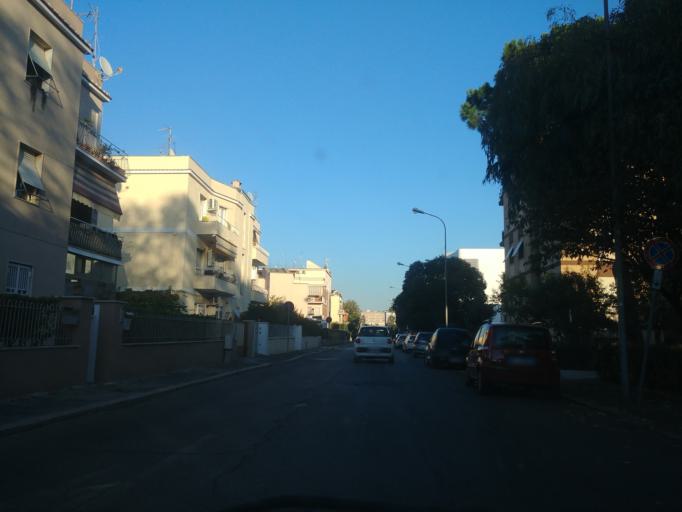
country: IT
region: Latium
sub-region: Provincia di Latina
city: Latina
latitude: 41.4603
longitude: 12.9011
